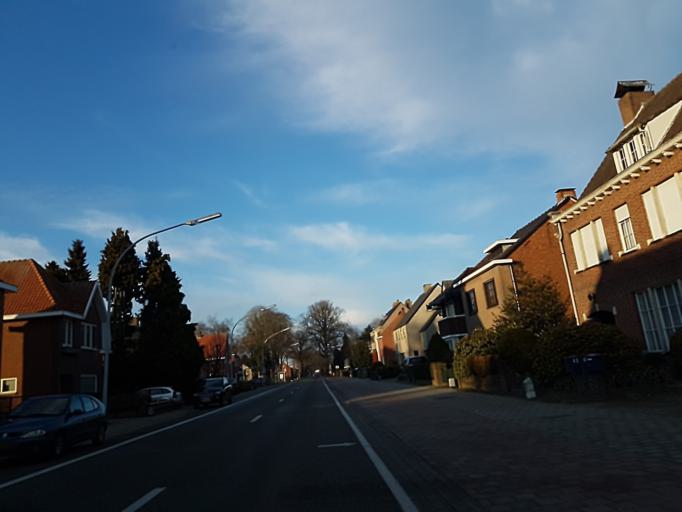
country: NL
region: North Brabant
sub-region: Gemeente Goirle
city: Goirle
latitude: 51.4508
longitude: 5.0439
